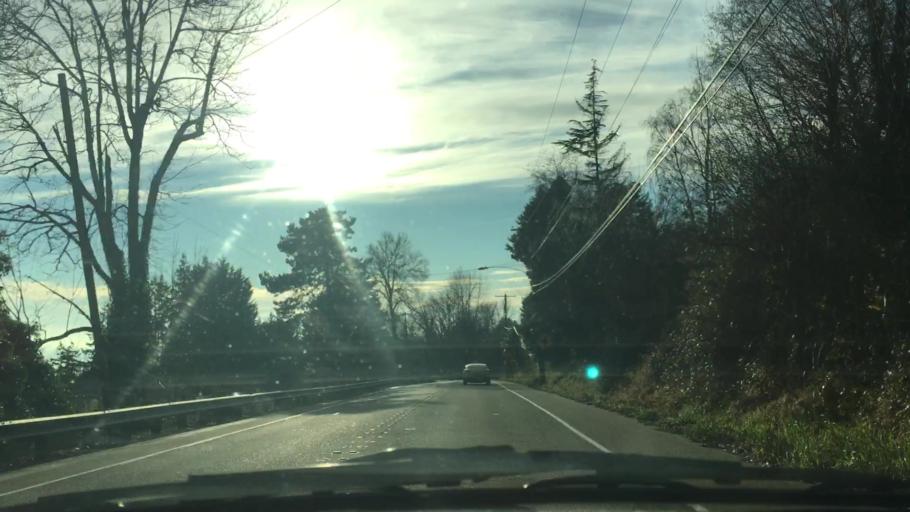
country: US
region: Washington
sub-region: King County
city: Des Moines
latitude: 47.4136
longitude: -122.3228
